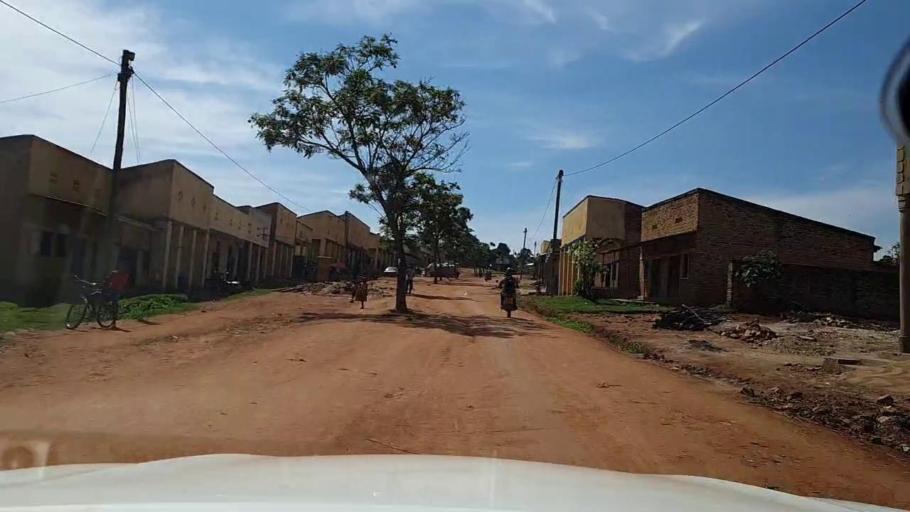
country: RW
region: Southern Province
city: Butare
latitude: -2.6883
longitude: 29.8539
